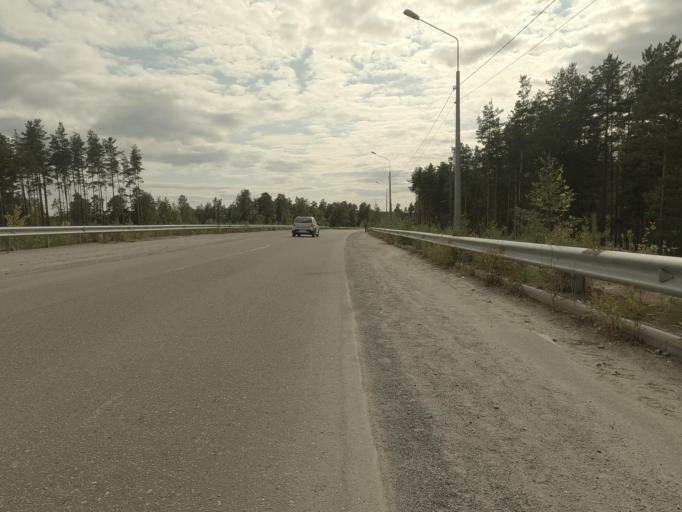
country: RU
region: Leningrad
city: Kamennogorsk
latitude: 60.9584
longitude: 29.1379
